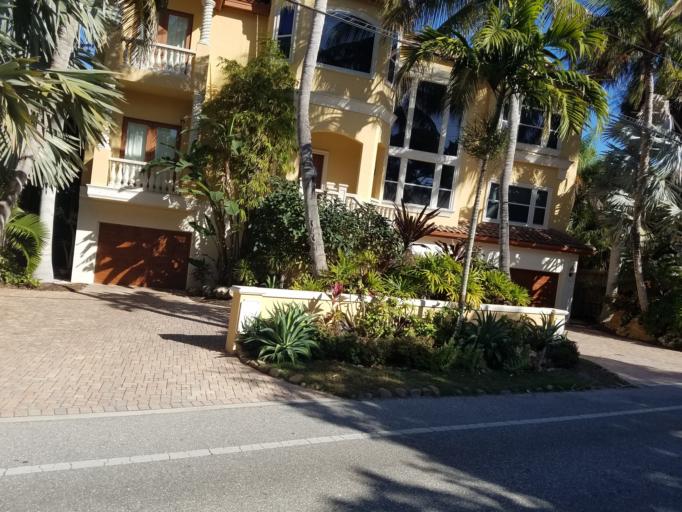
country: US
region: Florida
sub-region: Sarasota County
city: Gulf Gate Estates
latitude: 27.2374
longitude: -82.5244
